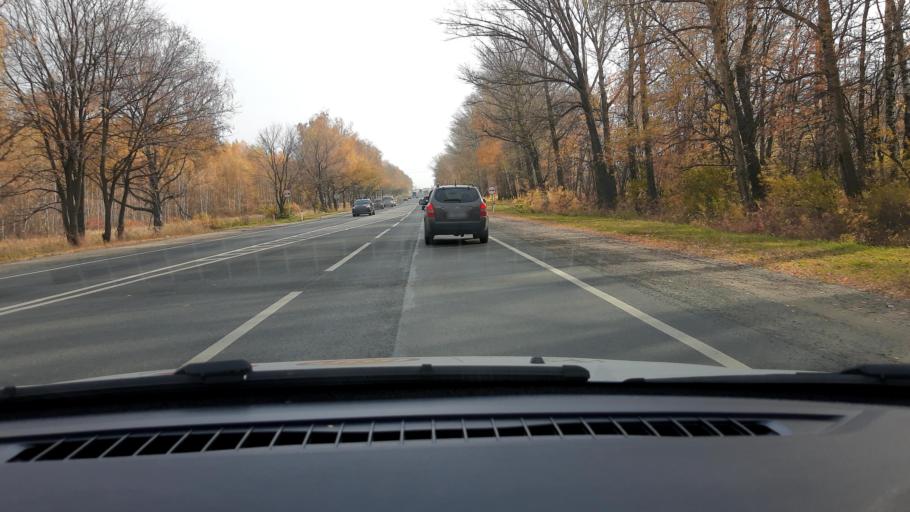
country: RU
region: Nizjnij Novgorod
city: Kstovo
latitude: 56.1387
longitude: 44.2335
